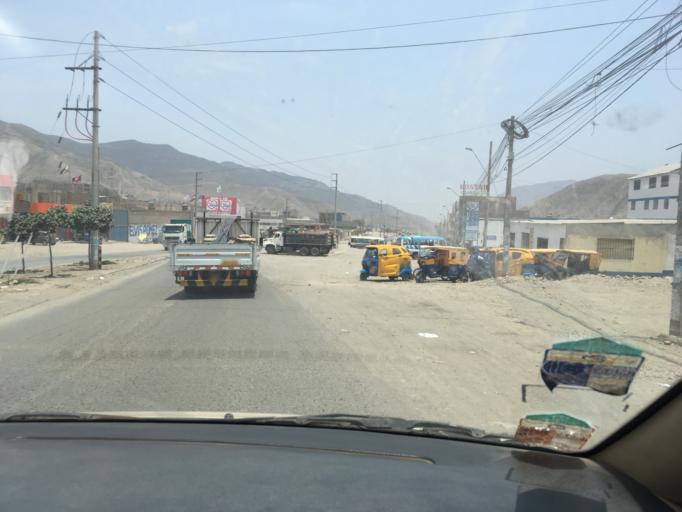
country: PE
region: Lima
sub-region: Lima
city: Cieneguilla
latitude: -12.1244
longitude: -76.8724
